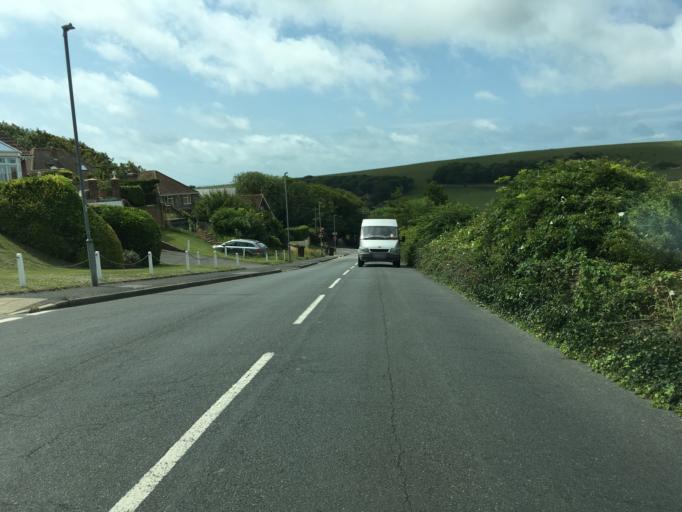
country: GB
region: England
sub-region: Brighton and Hove
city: Rottingdean
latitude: 50.8200
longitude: -0.0738
